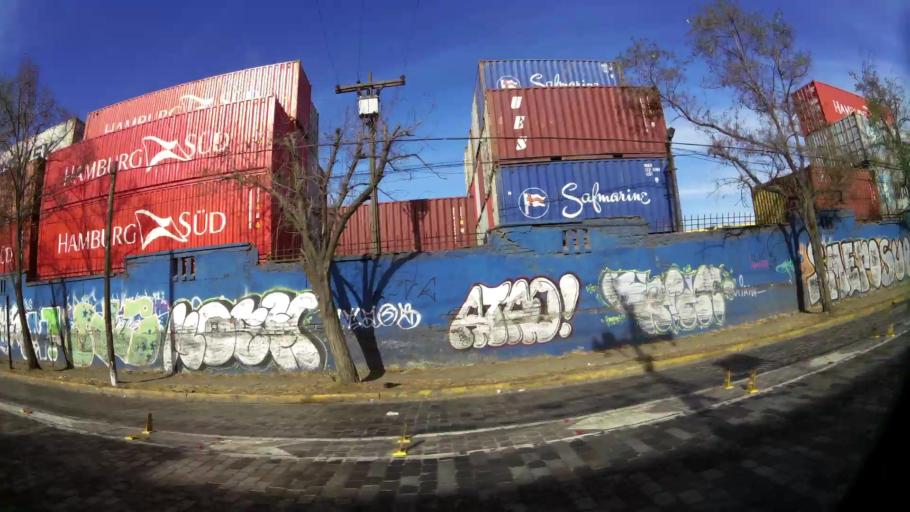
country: CL
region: Santiago Metropolitan
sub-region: Provincia de Santiago
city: Santiago
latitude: -33.4577
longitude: -70.6807
